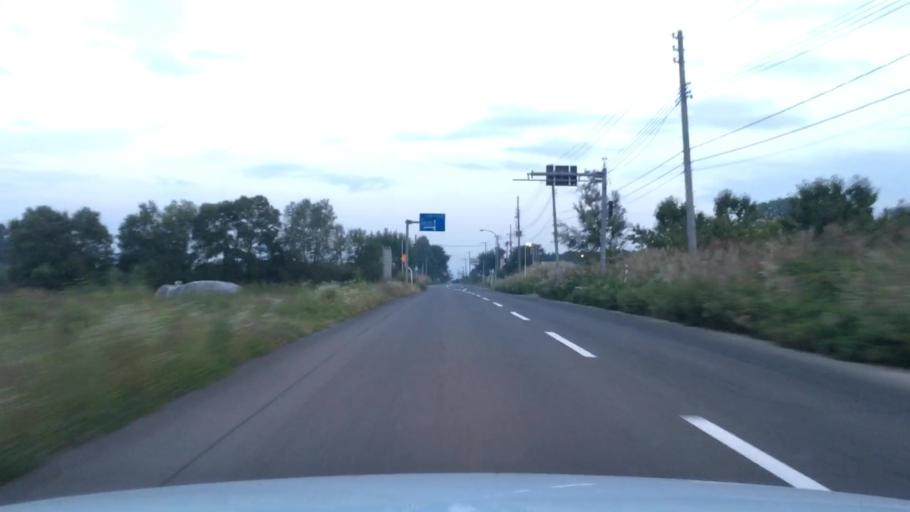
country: JP
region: Aomori
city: Hirosaki
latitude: 40.6791
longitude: 140.3727
